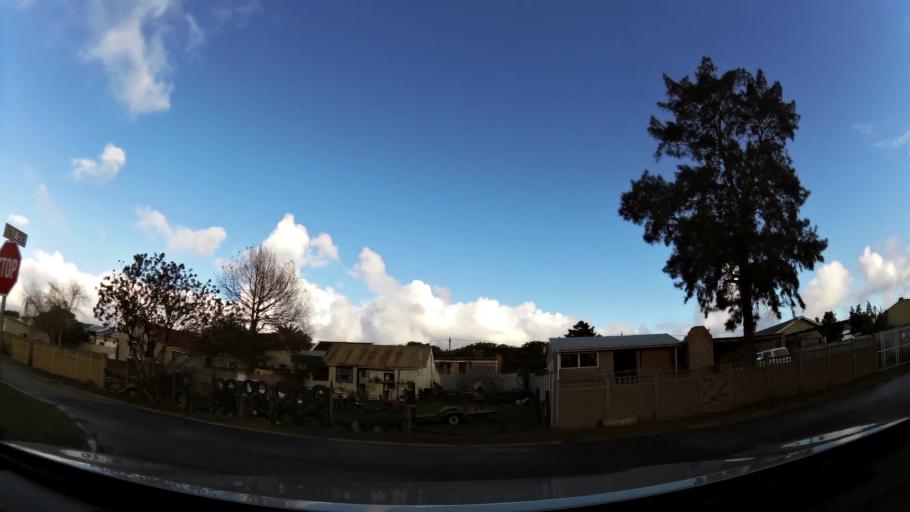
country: ZA
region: Western Cape
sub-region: Eden District Municipality
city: Riversdale
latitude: -34.2021
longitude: 21.5820
